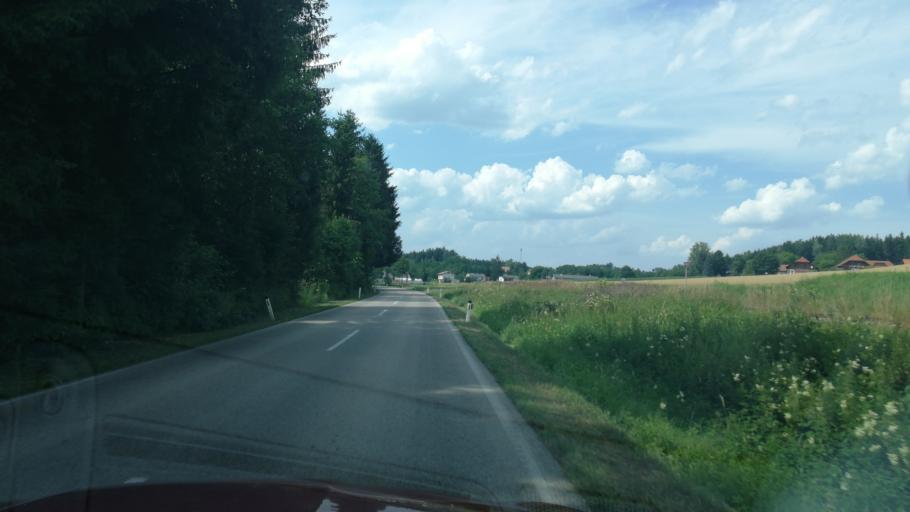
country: AT
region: Upper Austria
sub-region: Politischer Bezirk Vocklabruck
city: Puhret
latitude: 48.0317
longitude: 13.7036
